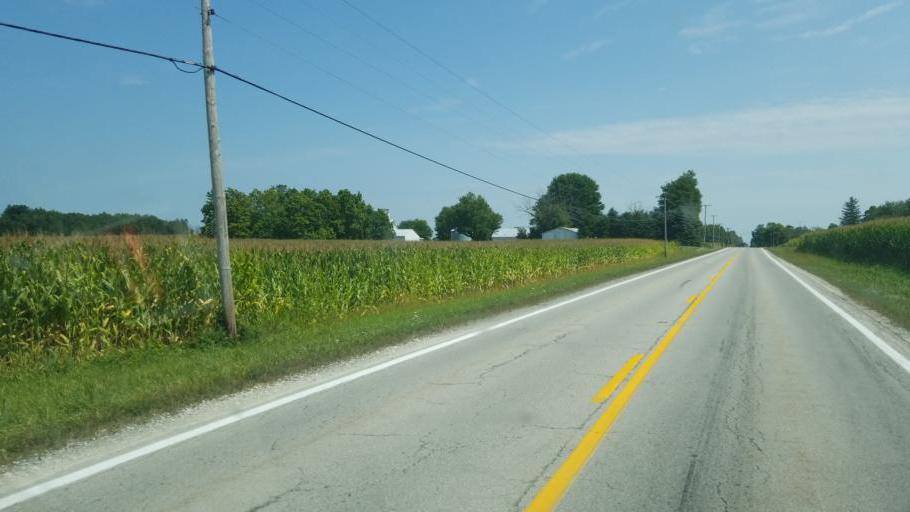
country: US
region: Ohio
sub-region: Marion County
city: Marion
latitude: 40.6878
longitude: -83.1657
